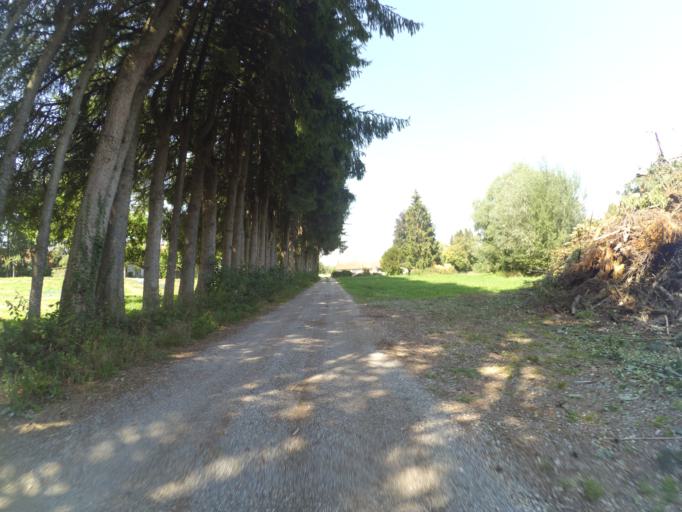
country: DE
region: Bavaria
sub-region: Swabia
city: Lamerdingen
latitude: 48.1084
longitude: 10.7740
